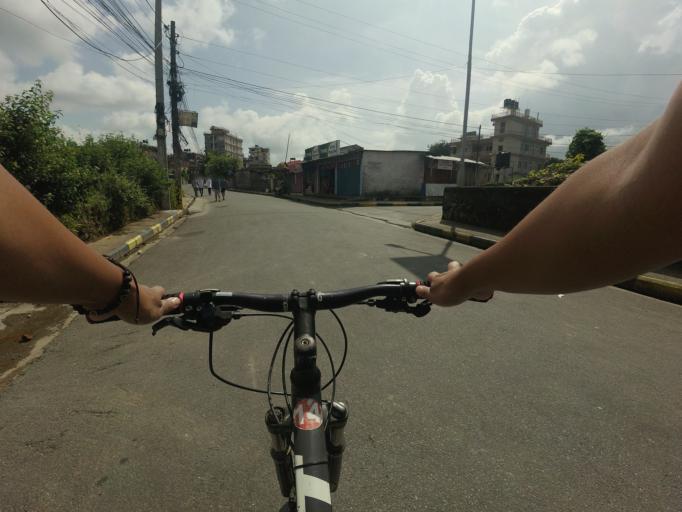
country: NP
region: Western Region
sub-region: Gandaki Zone
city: Pokhara
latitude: 28.2111
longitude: 83.9600
